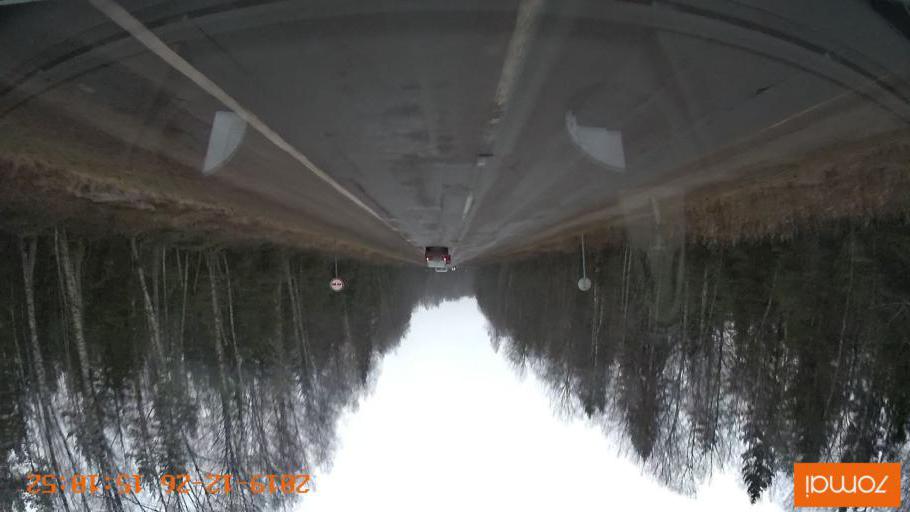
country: RU
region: Jaroslavl
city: Rybinsk
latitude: 58.1375
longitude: 38.8551
